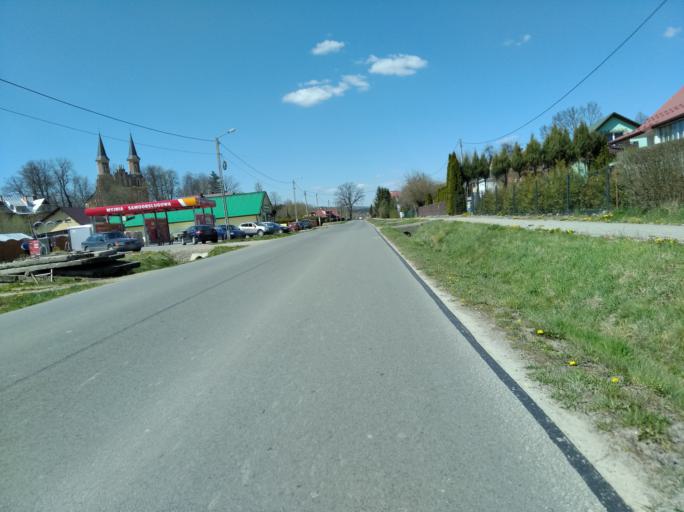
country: PL
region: Subcarpathian Voivodeship
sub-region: Powiat brzozowski
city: Dydnia
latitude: 49.6835
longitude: 22.1787
